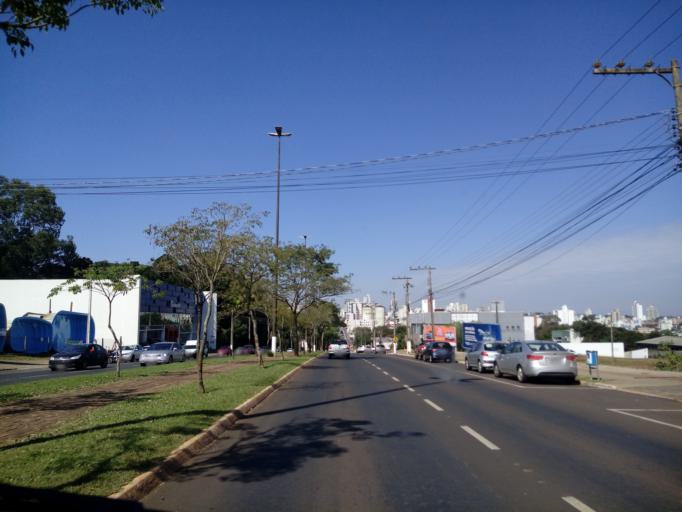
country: BR
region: Santa Catarina
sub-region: Chapeco
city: Chapeco
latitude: -27.0850
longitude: -52.6198
